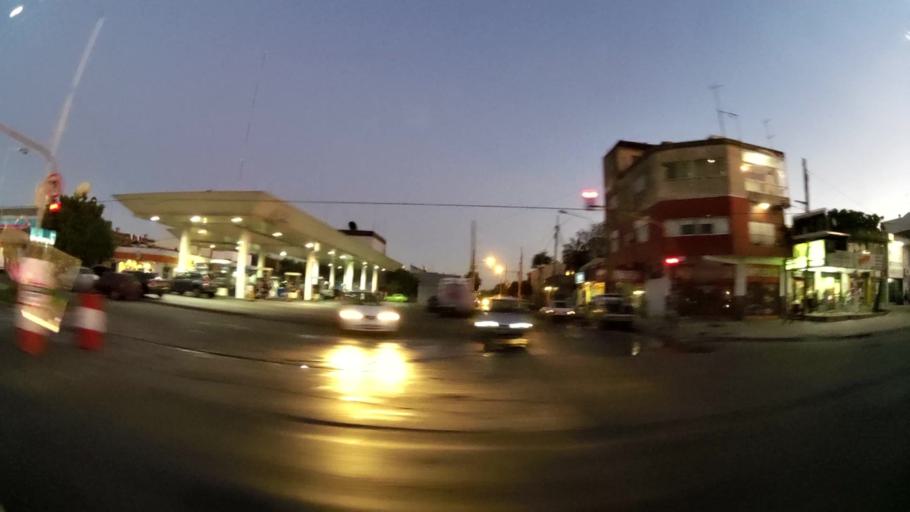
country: AR
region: Buenos Aires
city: San Justo
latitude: -34.7119
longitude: -58.5904
